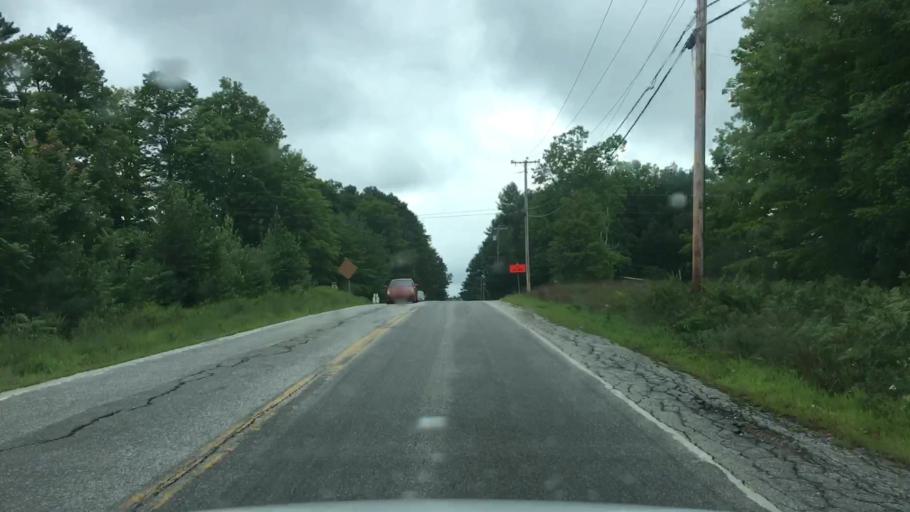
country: US
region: Maine
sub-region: York County
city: Cornish
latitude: 43.8191
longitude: -70.7714
